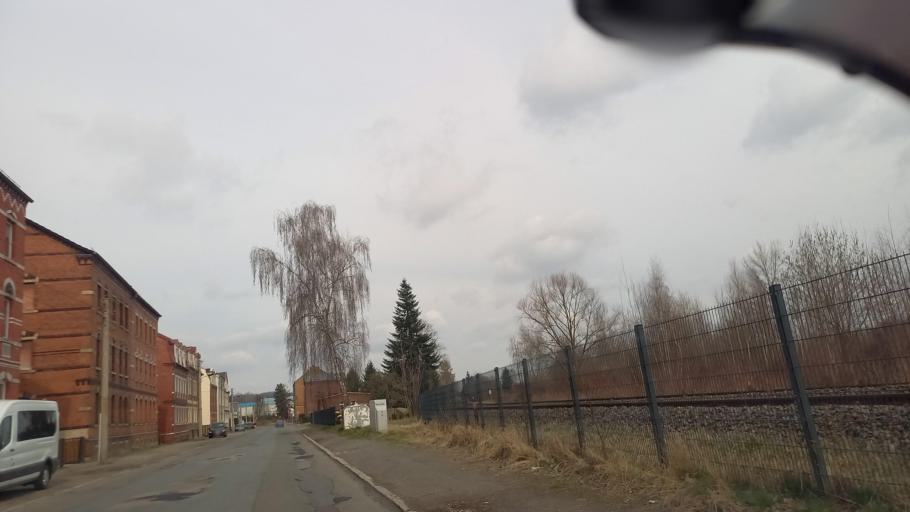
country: DE
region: Saxony
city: Wilkau-Hasslau
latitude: 50.6788
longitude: 12.5027
